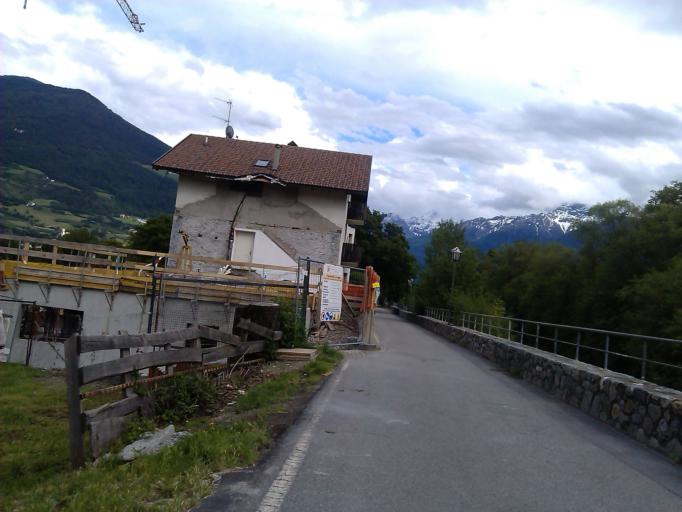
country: IT
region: Trentino-Alto Adige
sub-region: Bolzano
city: Glorenza
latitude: 46.6695
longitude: 10.5540
